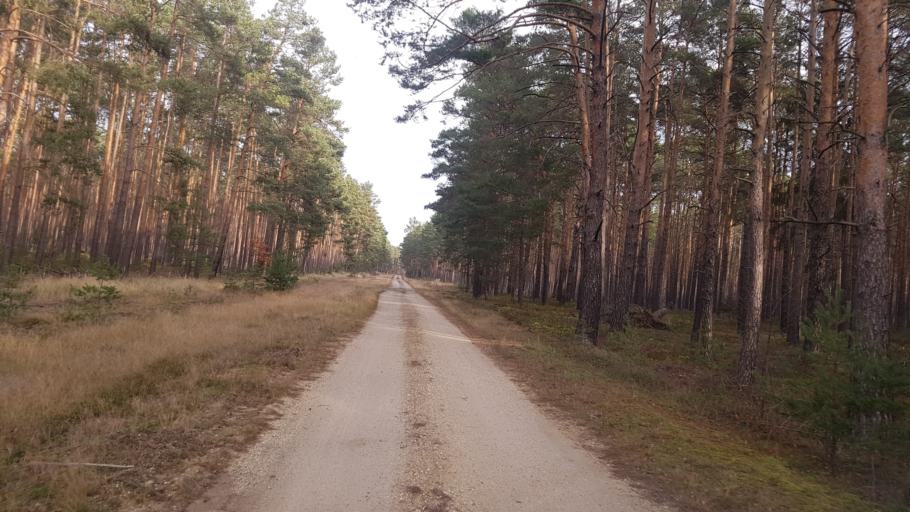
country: DE
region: Brandenburg
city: Schonborn
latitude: 51.5711
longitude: 13.4698
